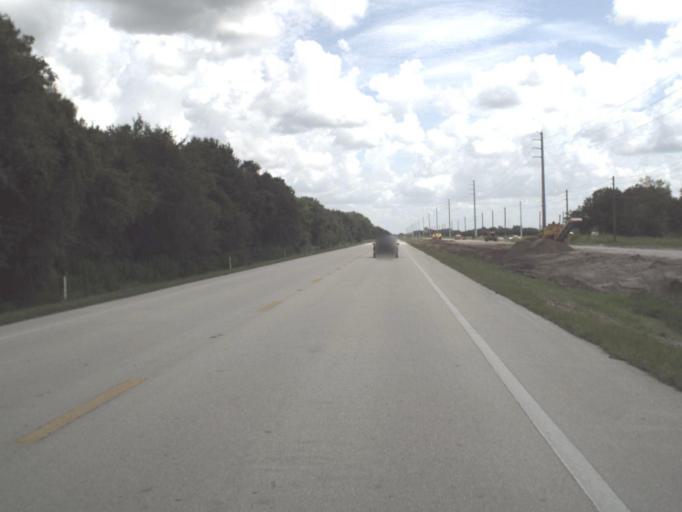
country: US
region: Florida
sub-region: DeSoto County
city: Nocatee
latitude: 27.1071
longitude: -81.9306
